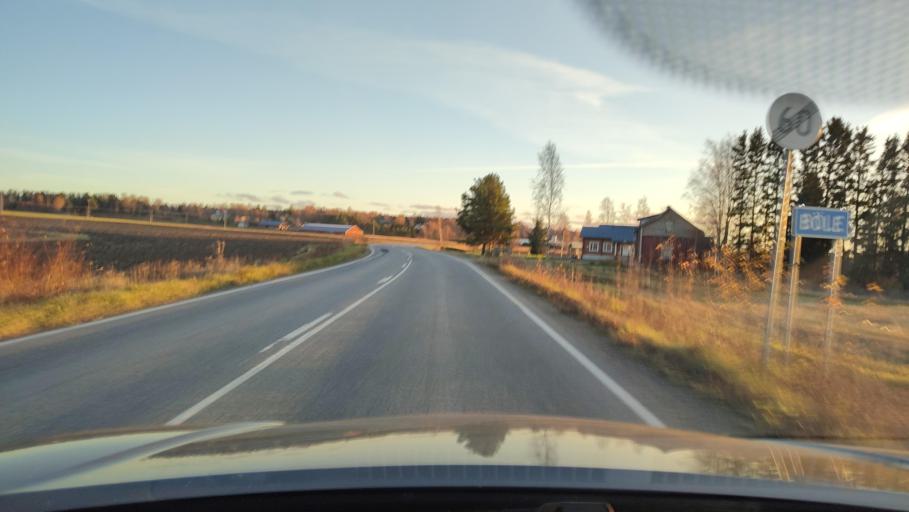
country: FI
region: Ostrobothnia
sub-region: Sydosterbotten
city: Naerpes
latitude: 62.4405
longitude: 21.3513
